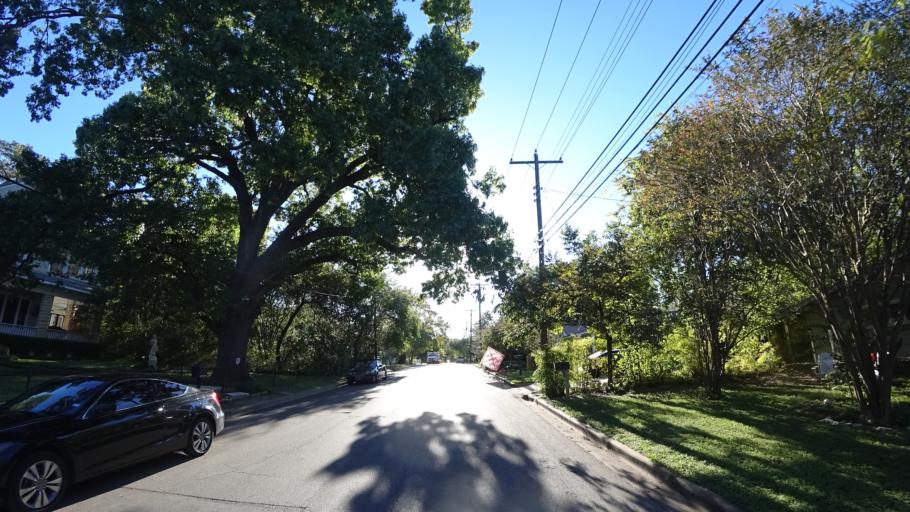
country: US
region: Texas
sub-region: Travis County
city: Austin
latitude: 30.3089
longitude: -97.7212
